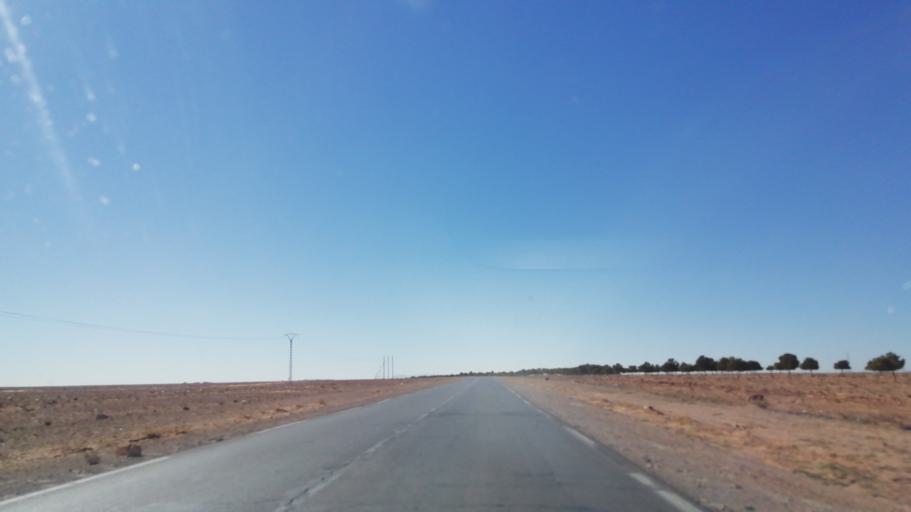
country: DZ
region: Saida
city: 'Ain el Hadjar
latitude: 34.0038
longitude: 0.0462
